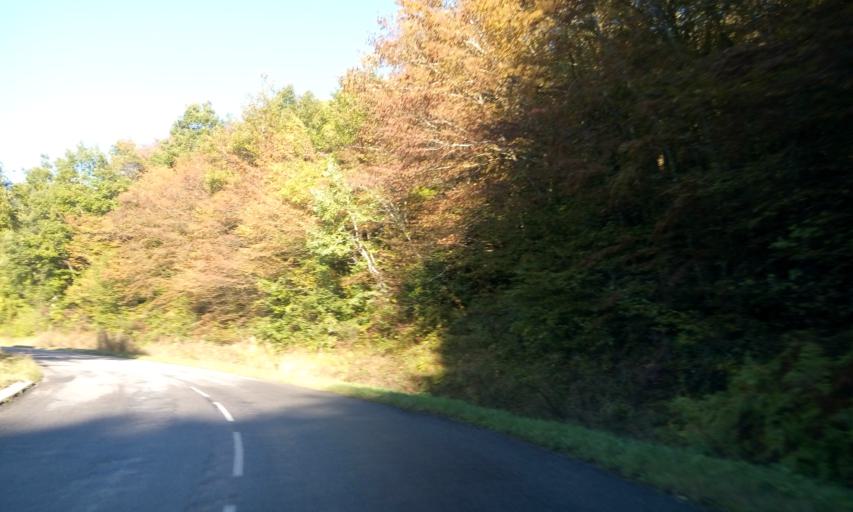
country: FR
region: Rhone-Alpes
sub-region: Departement du Rhone
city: Tarare
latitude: 45.9130
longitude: 4.4397
